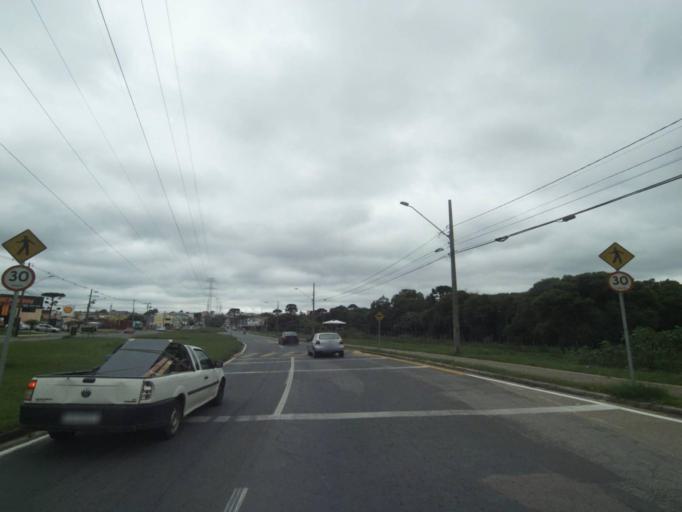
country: BR
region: Parana
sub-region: Araucaria
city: Araucaria
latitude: -25.5554
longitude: -49.3330
